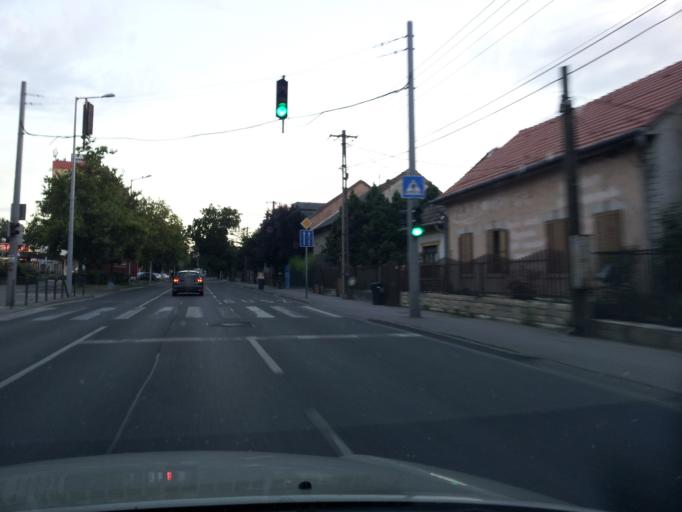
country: HU
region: Budapest
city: Budapest XV. keruelet
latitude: 47.5366
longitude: 19.1342
